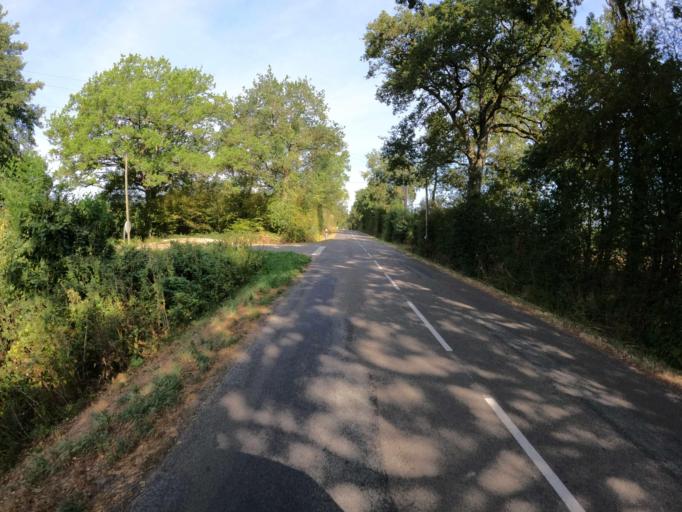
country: FR
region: Pays de la Loire
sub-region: Departement de la Vendee
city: Saint-Christophe-du-Ligneron
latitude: 46.8054
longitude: -1.8004
